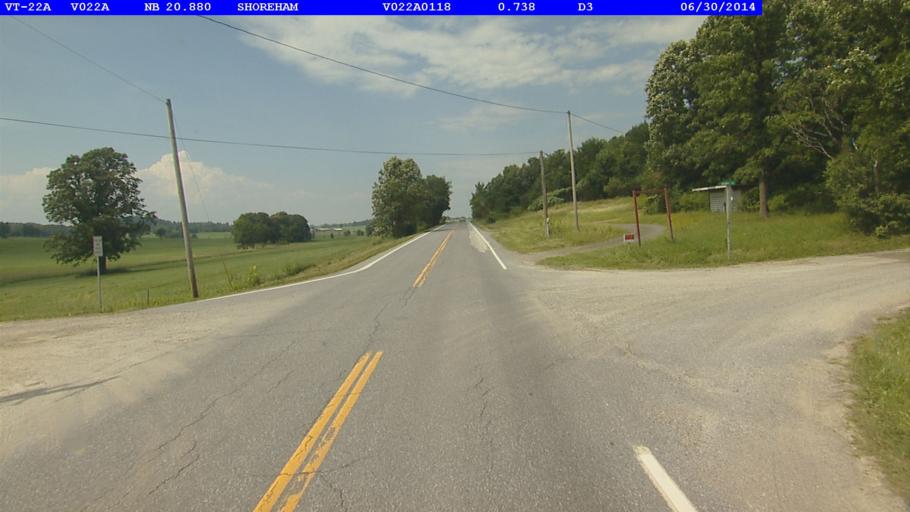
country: US
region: New York
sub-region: Essex County
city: Ticonderoga
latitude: 43.8601
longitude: -73.3094
